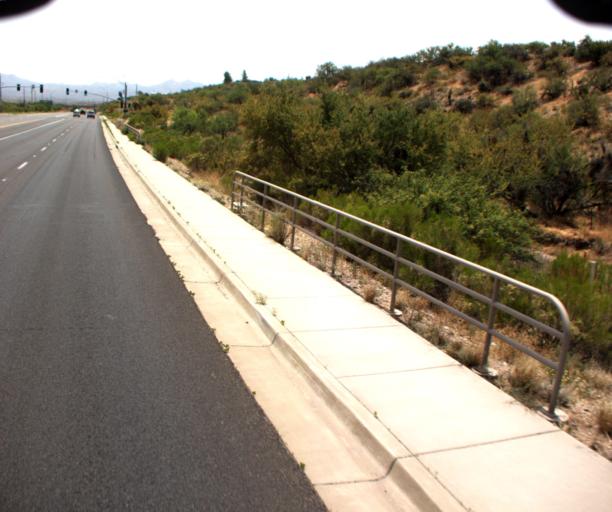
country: US
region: Arizona
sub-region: Gila County
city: Globe
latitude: 33.3800
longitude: -110.7497
